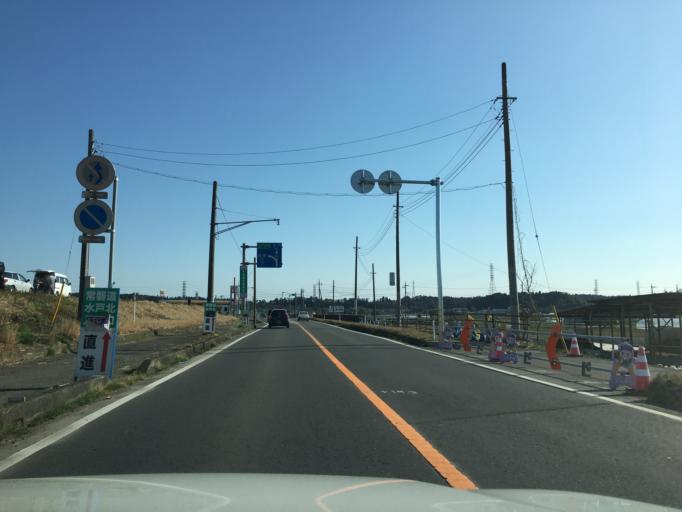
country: JP
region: Ibaraki
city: Mito-shi
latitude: 36.4256
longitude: 140.4217
